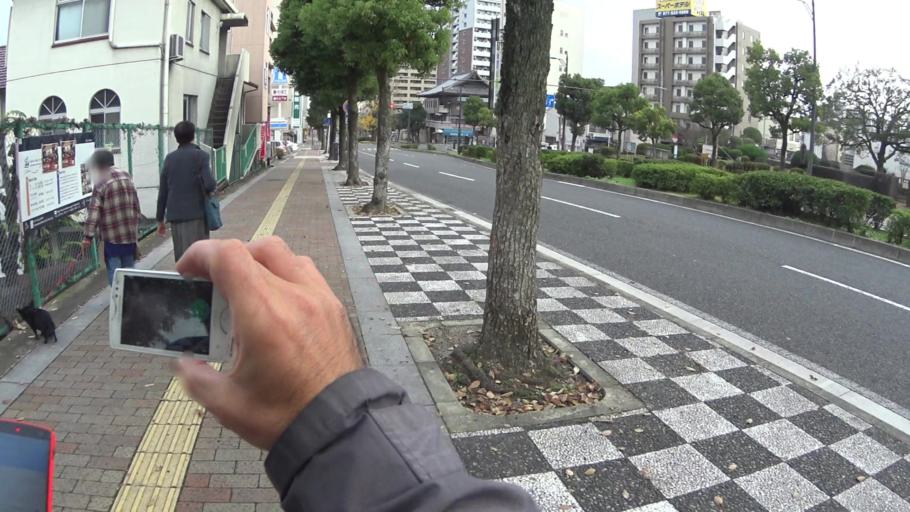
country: JP
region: Shiga Prefecture
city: Otsu-shi
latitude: 35.0052
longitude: 135.8654
